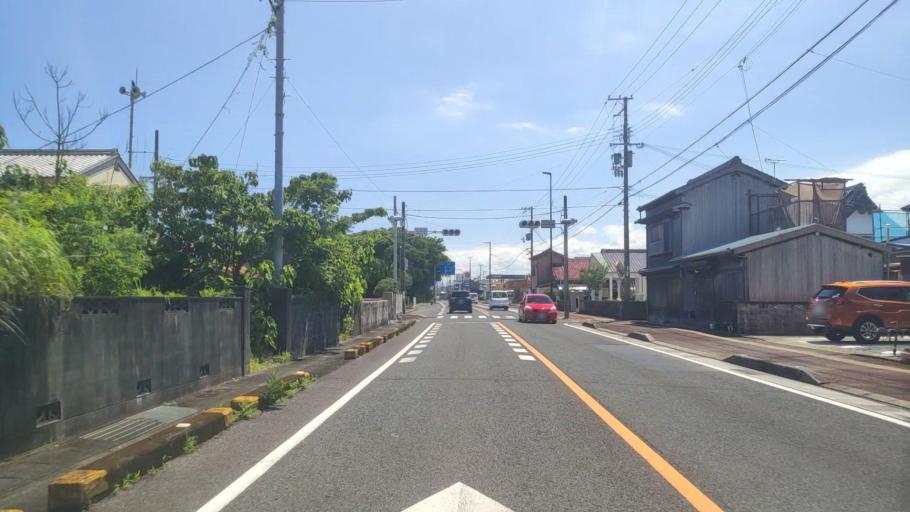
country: JP
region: Wakayama
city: Shingu
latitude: 33.8725
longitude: 136.0859
